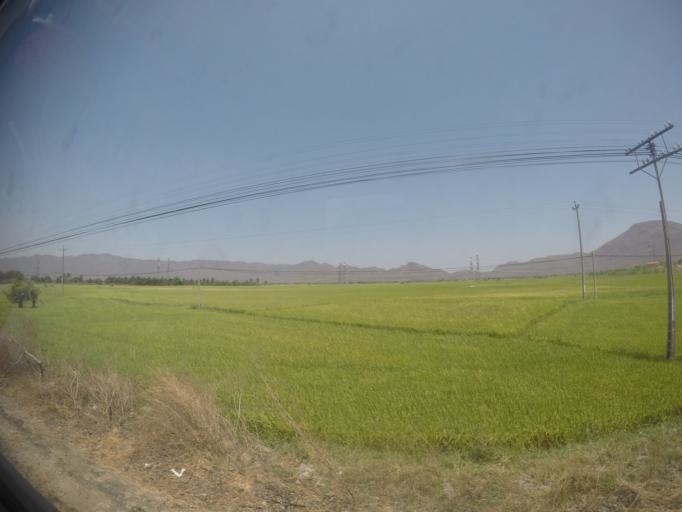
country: VN
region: Binh Thuan
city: Lien Huong
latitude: 11.2626
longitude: 108.6696
